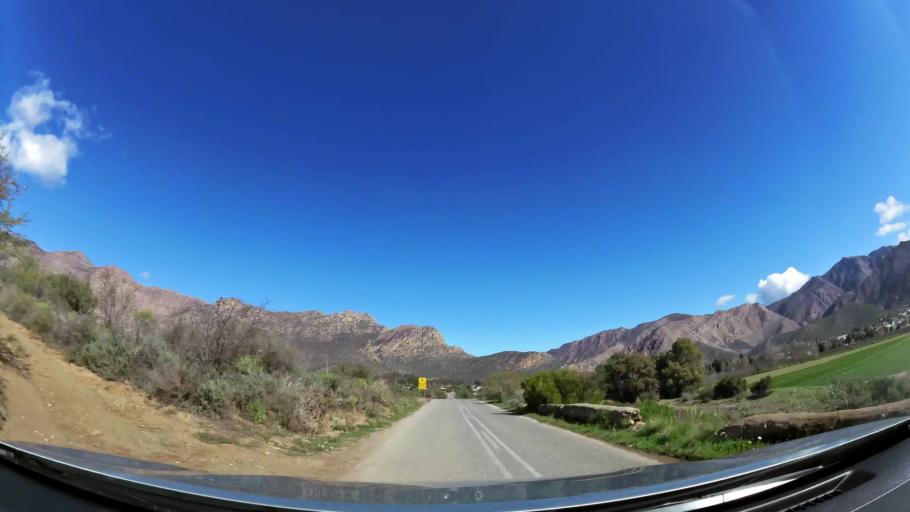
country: ZA
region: Western Cape
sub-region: Cape Winelands District Municipality
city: Ashton
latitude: -33.7901
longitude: 20.1313
